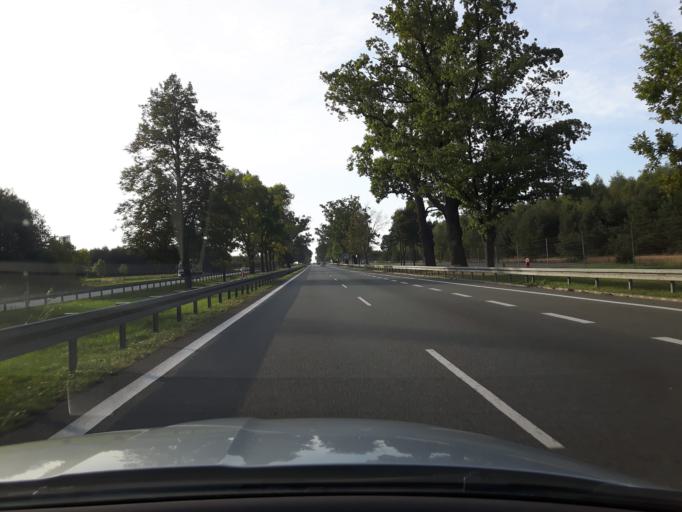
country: PL
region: Masovian Voivodeship
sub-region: Powiat bialobrzeski
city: Sucha
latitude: 51.5973
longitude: 20.9906
